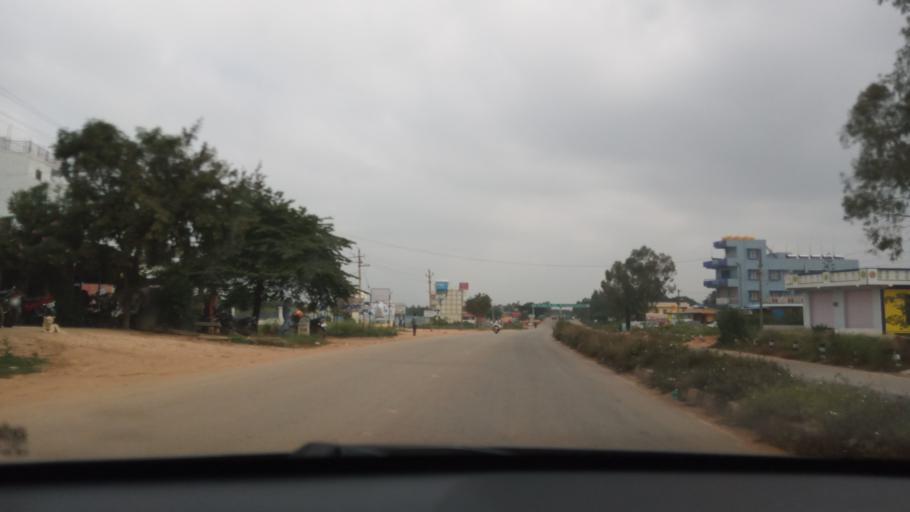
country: IN
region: Karnataka
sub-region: Bangalore Rural
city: Vijayapura
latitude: 13.2459
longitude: 77.9328
